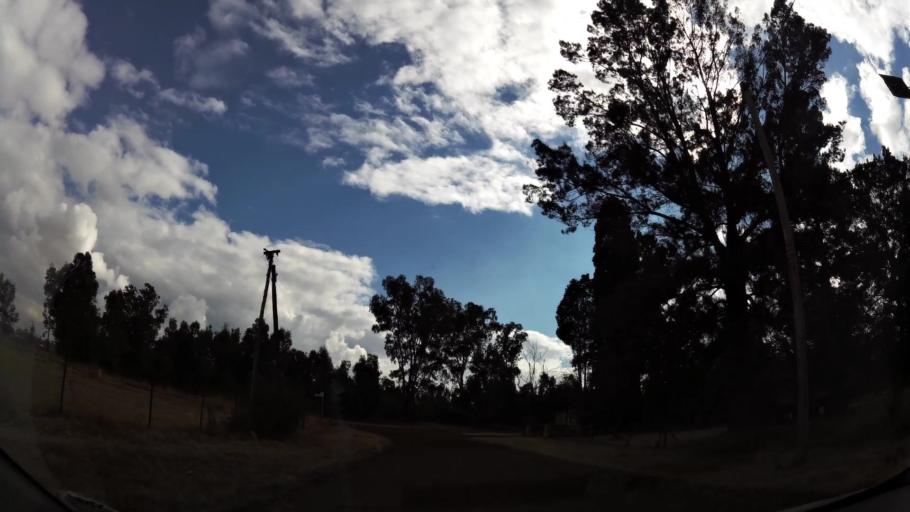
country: ZA
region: Gauteng
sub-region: Sedibeng District Municipality
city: Meyerton
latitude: -26.5962
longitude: 28.0916
